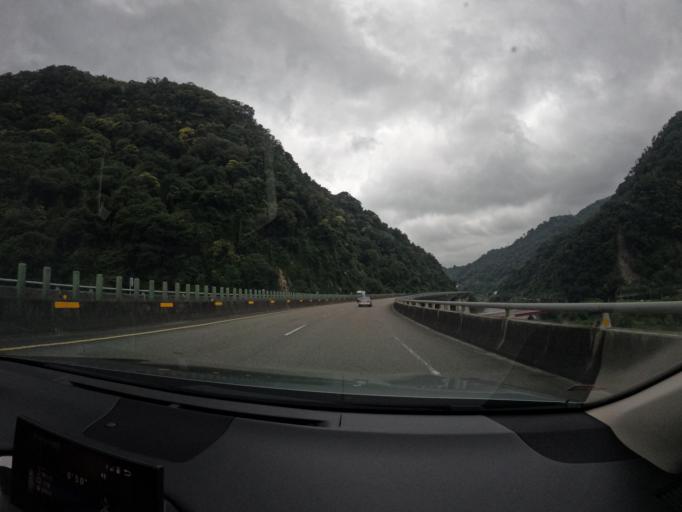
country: TW
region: Taiwan
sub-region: Miaoli
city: Miaoli
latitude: 24.4610
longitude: 120.8551
